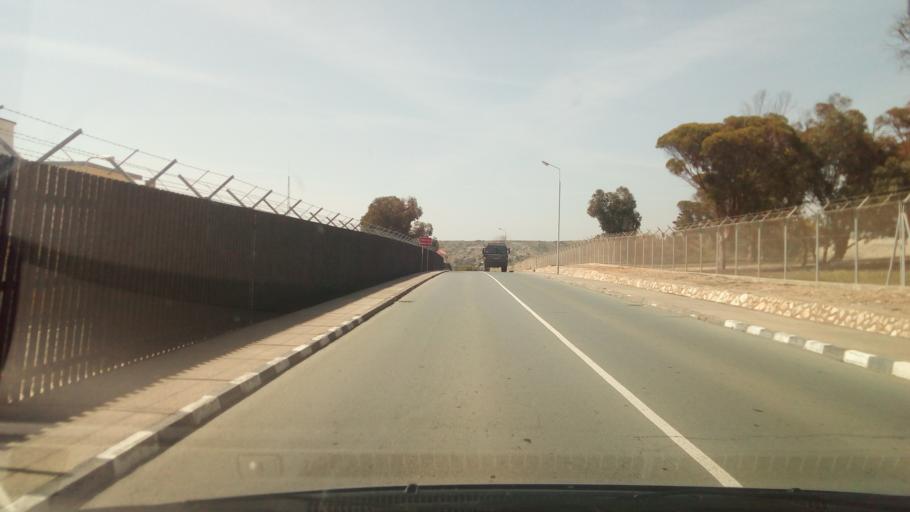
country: CY
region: Larnaka
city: Xylotymbou
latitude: 34.9823
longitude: 33.7236
